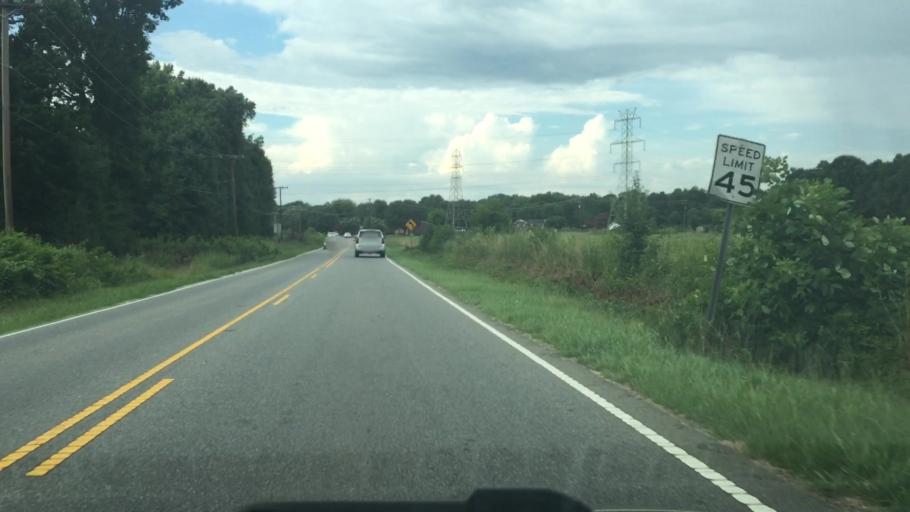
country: US
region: North Carolina
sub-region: Cabarrus County
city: Harrisburg
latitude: 35.4183
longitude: -80.7093
